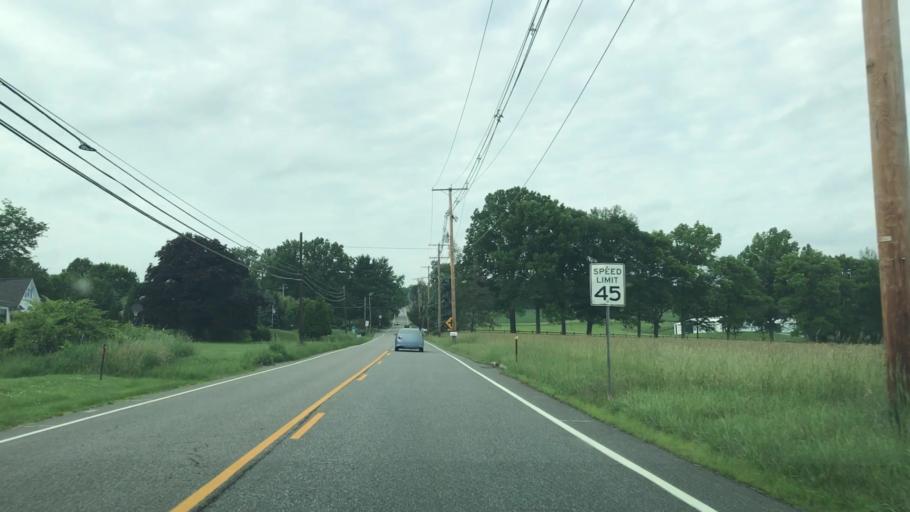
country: US
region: New Jersey
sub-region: Hunterdon County
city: Lebanon
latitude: 40.6566
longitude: -74.8292
